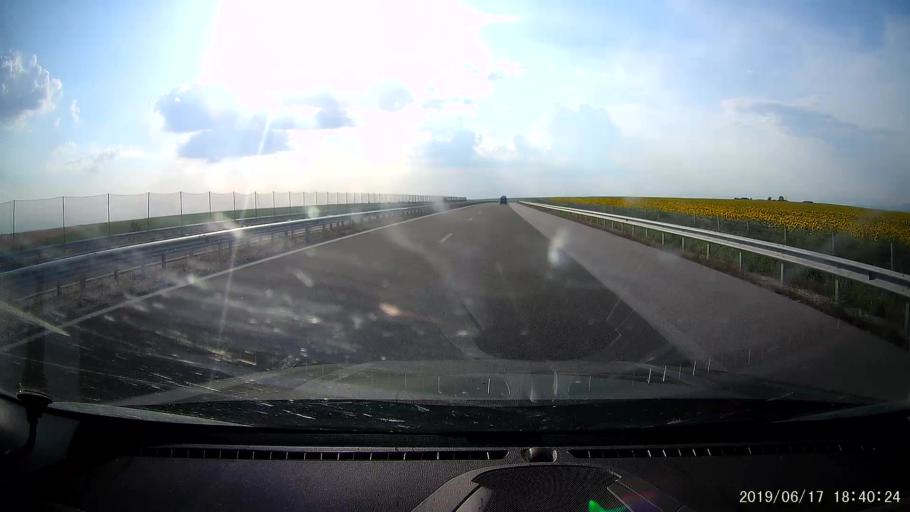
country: BG
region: Stara Zagora
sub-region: Obshtina Chirpan
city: Chirpan
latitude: 42.1550
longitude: 25.2789
